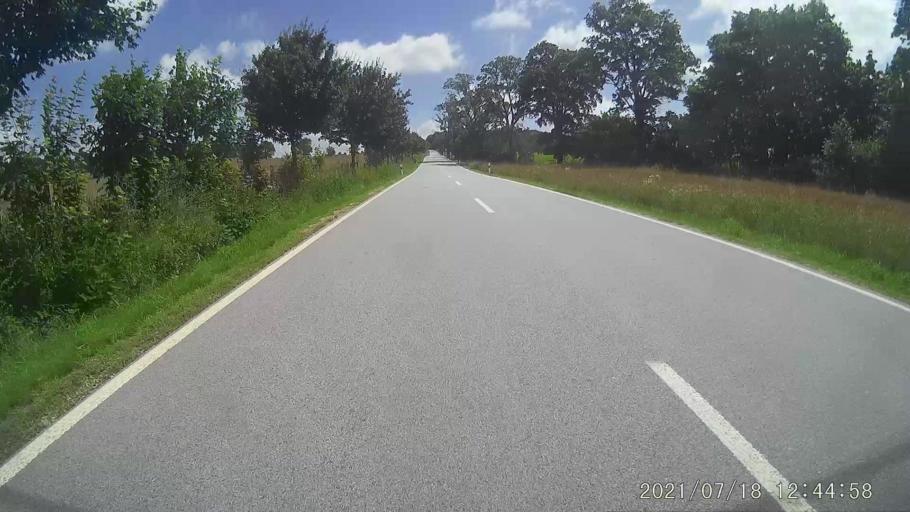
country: DE
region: Saxony
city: Reichenbach
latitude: 51.1866
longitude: 14.8010
